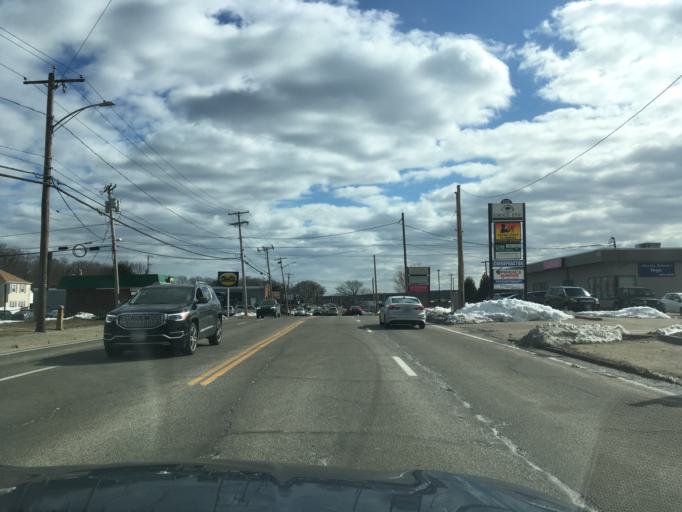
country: US
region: Rhode Island
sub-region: Kent County
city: West Warwick
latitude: 41.7357
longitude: -71.4779
